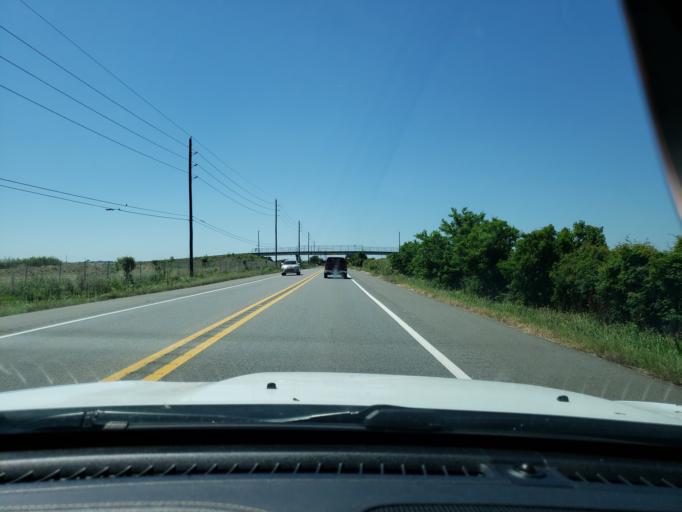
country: US
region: Texas
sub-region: Fort Bend County
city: Fulshear
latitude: 29.6836
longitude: -95.8391
